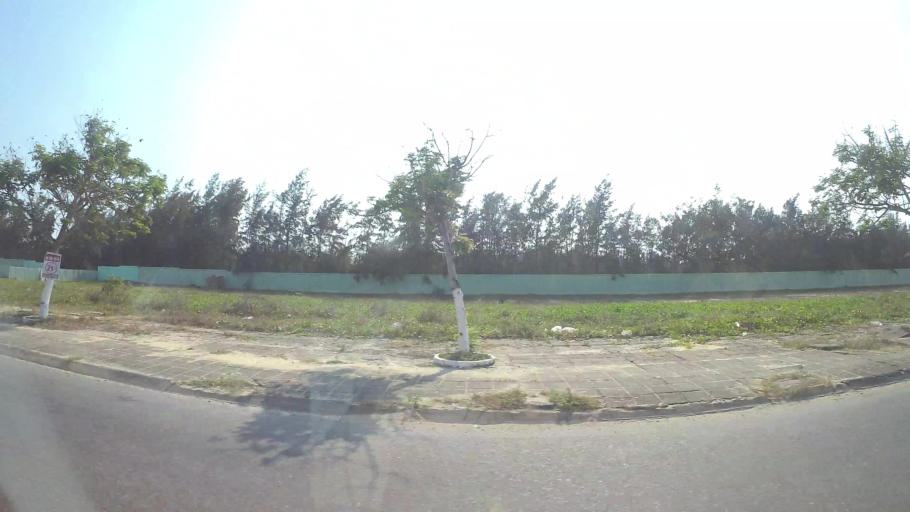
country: VN
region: Da Nang
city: Ngu Hanh Son
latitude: 15.9609
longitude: 108.2892
